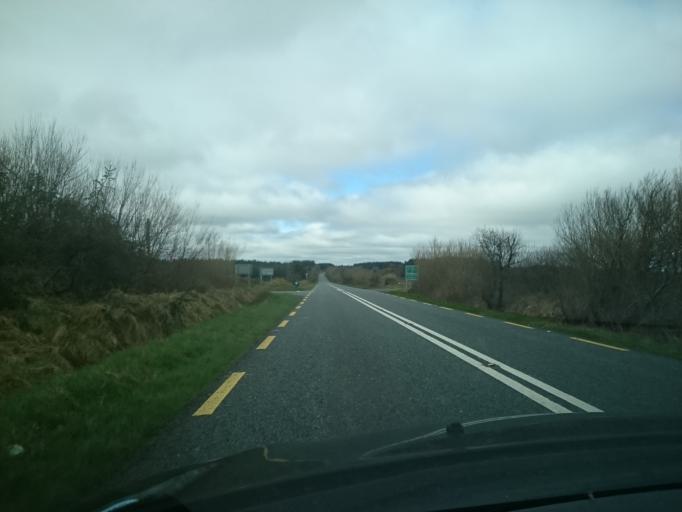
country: IE
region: Connaught
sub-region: Maigh Eo
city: Claremorris
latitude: 53.7160
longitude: -8.9010
